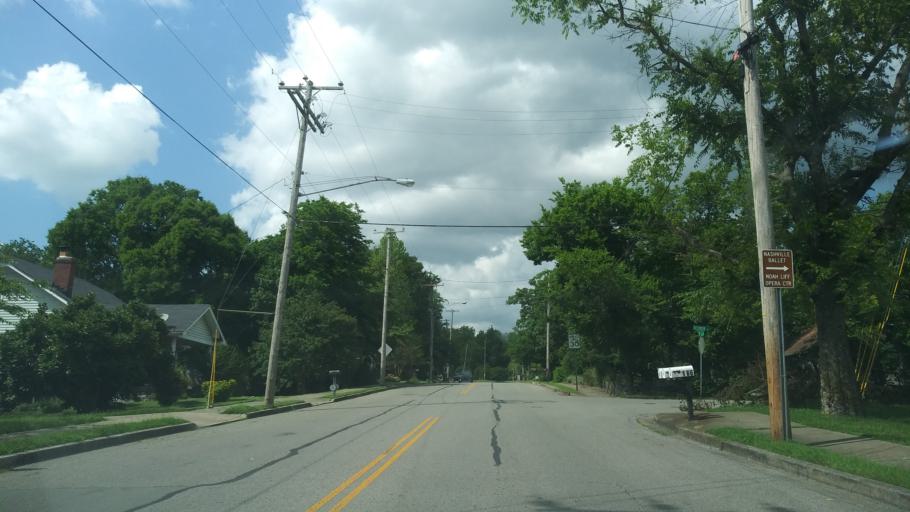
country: US
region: Tennessee
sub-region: Davidson County
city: Nashville
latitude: 36.1450
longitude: -86.8288
